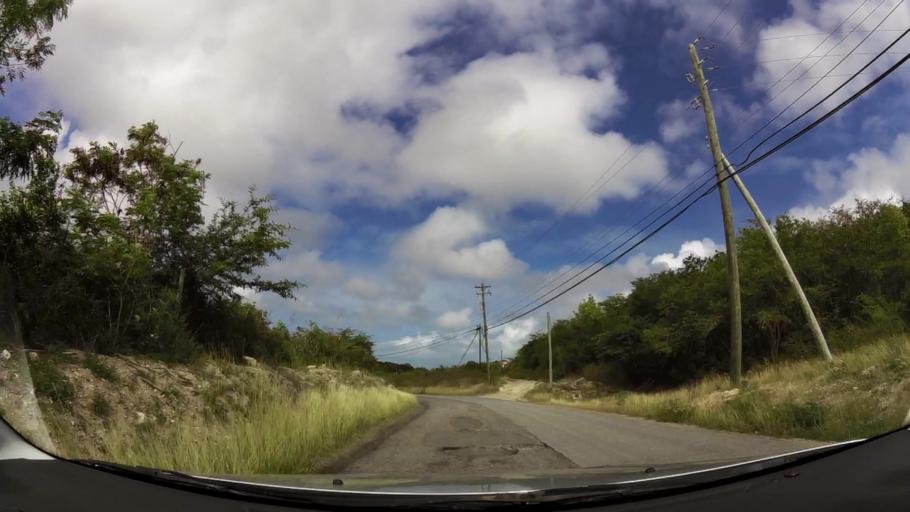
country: AG
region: Saint Paul
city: Liberta
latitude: 17.0522
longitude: -61.7284
